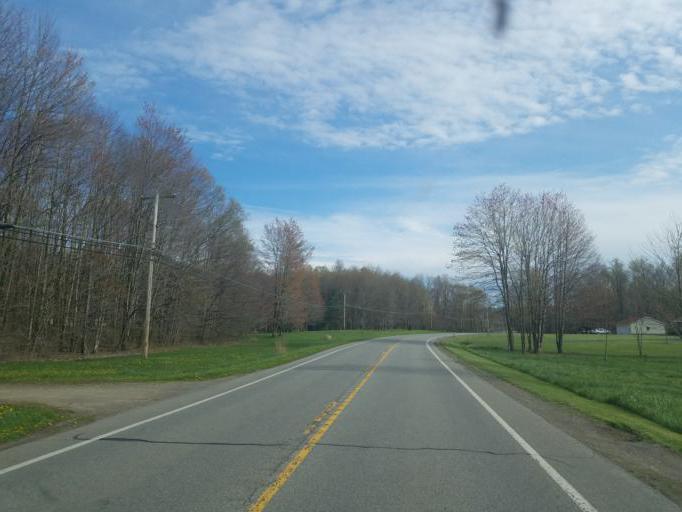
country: US
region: Pennsylvania
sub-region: Mercer County
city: Stoneboro
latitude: 41.3871
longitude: -80.0701
